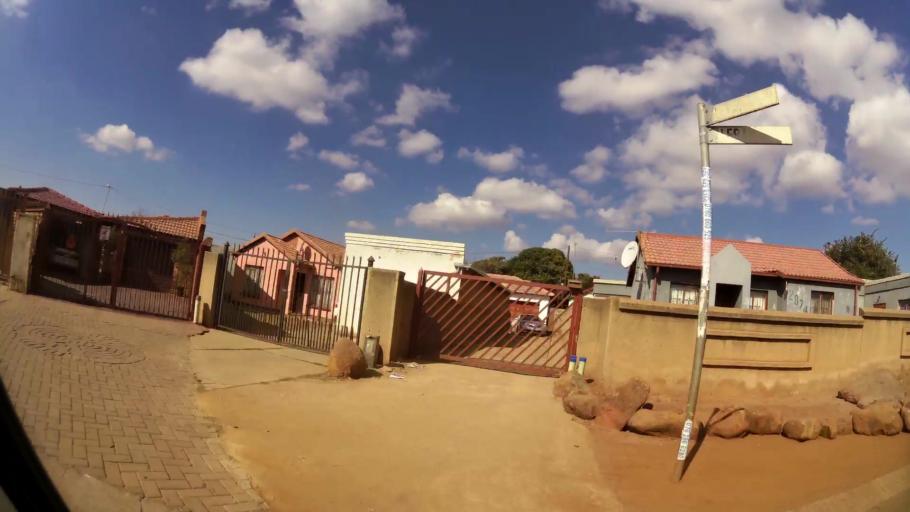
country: ZA
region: Gauteng
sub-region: City of Tshwane Metropolitan Municipality
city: Cullinan
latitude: -25.7029
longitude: 28.4180
